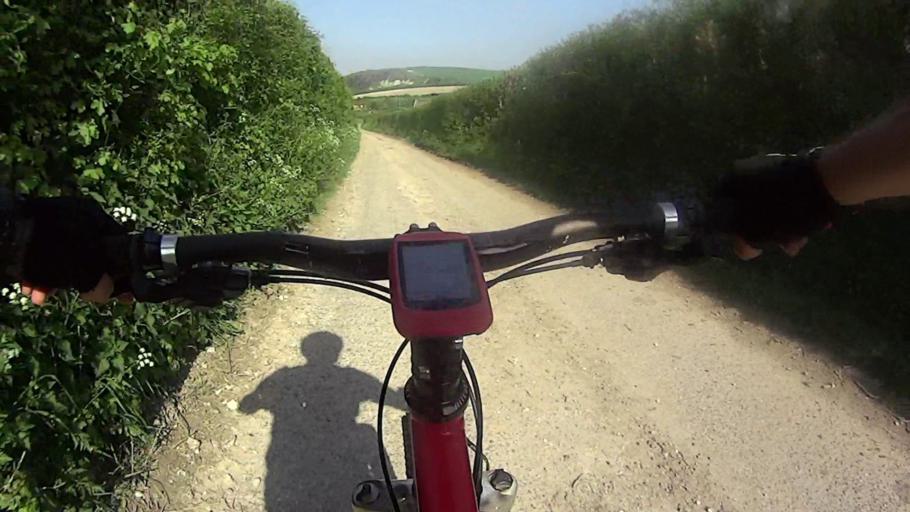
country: GB
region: England
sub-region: West Sussex
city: Midhurst
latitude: 50.9433
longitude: -0.7612
